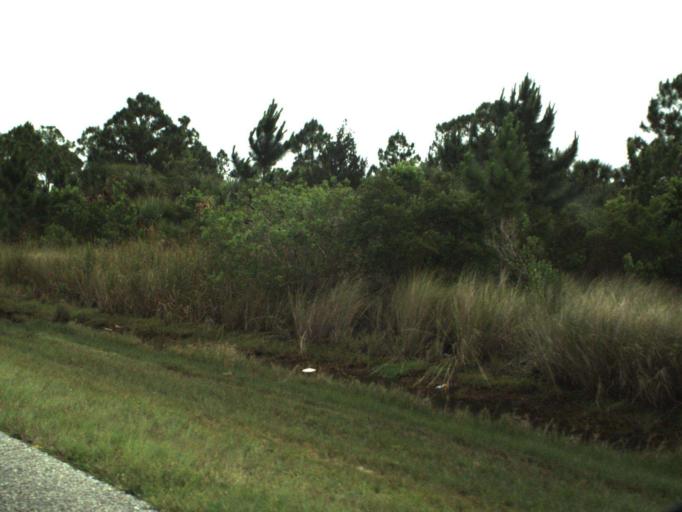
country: US
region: Florida
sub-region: Brevard County
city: Titusville
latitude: 28.5507
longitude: -80.8783
